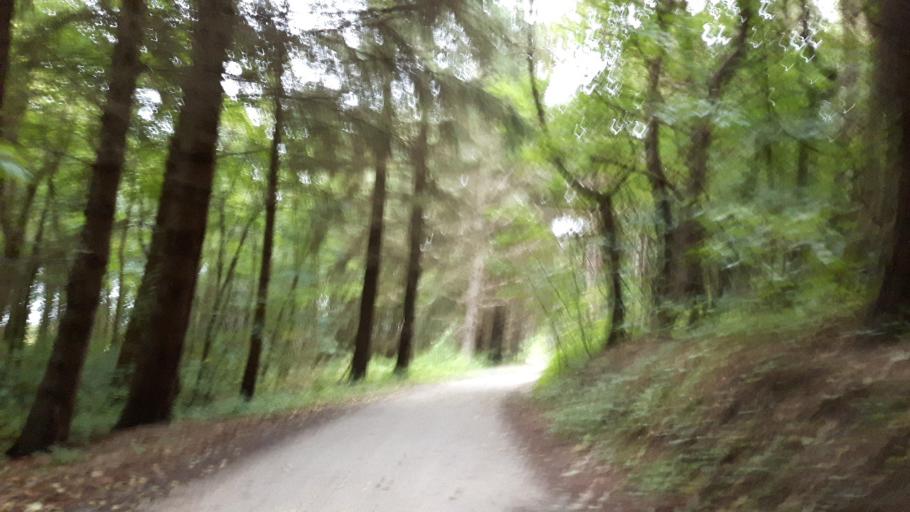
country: NL
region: Friesland
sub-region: Gemeente Ameland
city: Nes
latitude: 53.4538
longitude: 5.7568
